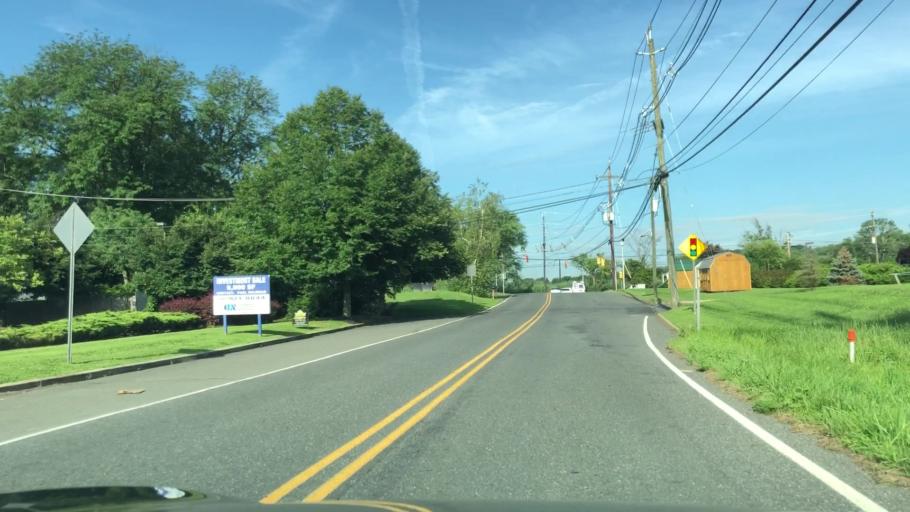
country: US
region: New Jersey
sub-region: Mercer County
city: Pennington
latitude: 40.3489
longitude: -74.7954
